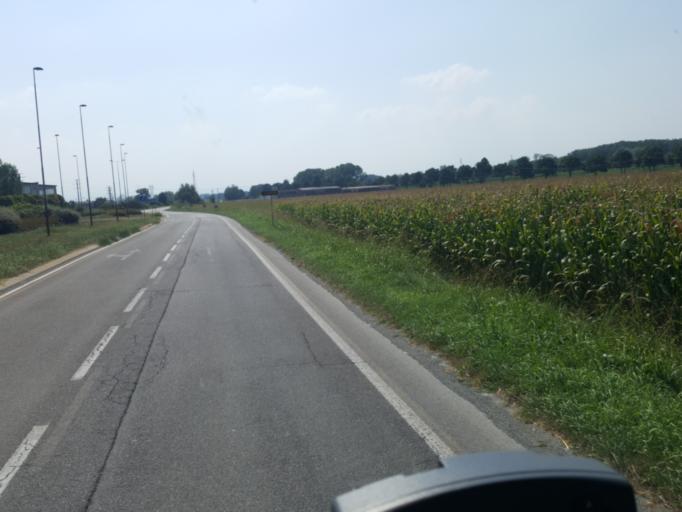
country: IT
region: Emilia-Romagna
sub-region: Provincia di Piacenza
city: Caorso
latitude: 45.0716
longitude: 9.8957
